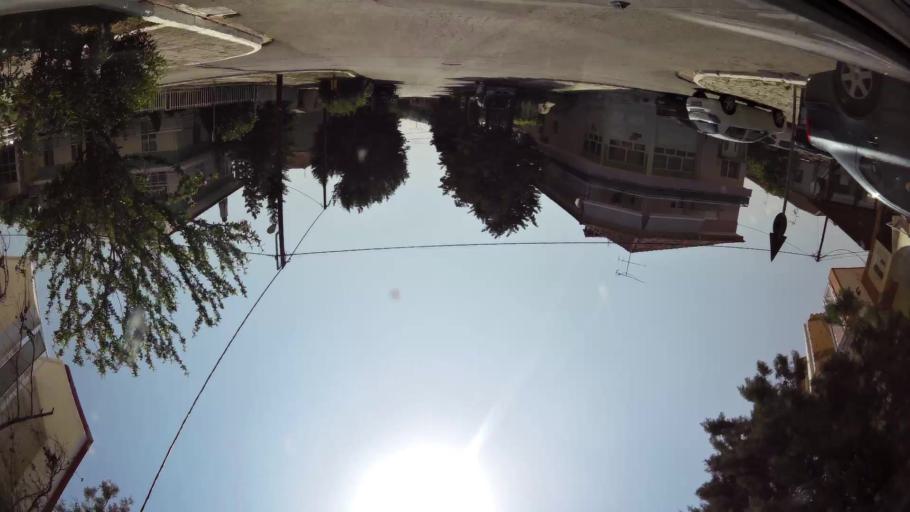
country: GR
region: West Macedonia
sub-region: Nomos Kozanis
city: Koila
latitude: 40.3361
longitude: 21.7901
